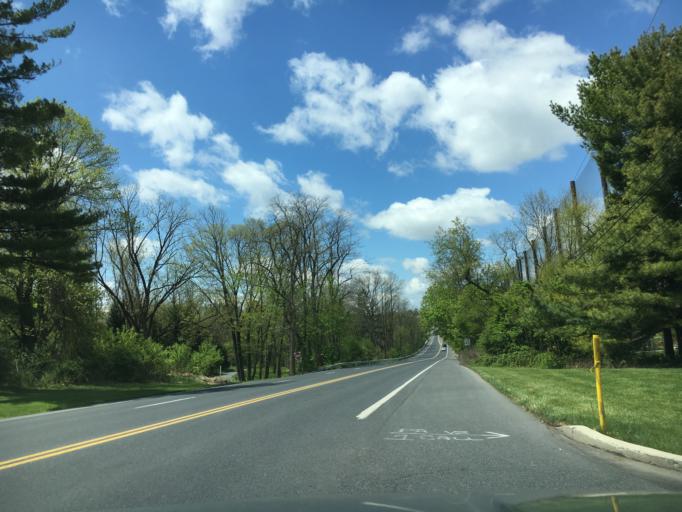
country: US
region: Pennsylvania
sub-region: Lehigh County
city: Dorneyville
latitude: 40.5966
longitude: -75.5318
